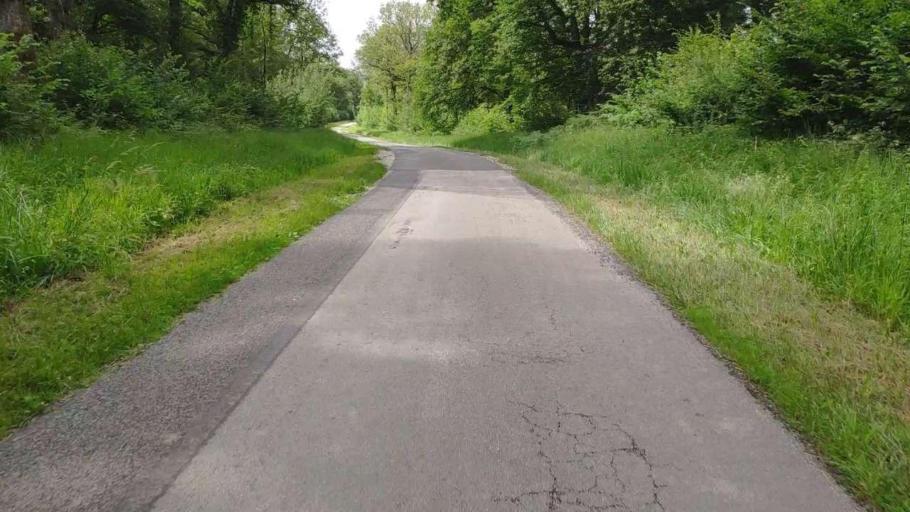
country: FR
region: Franche-Comte
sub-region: Departement du Jura
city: Bletterans
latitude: 46.8114
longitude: 5.4384
